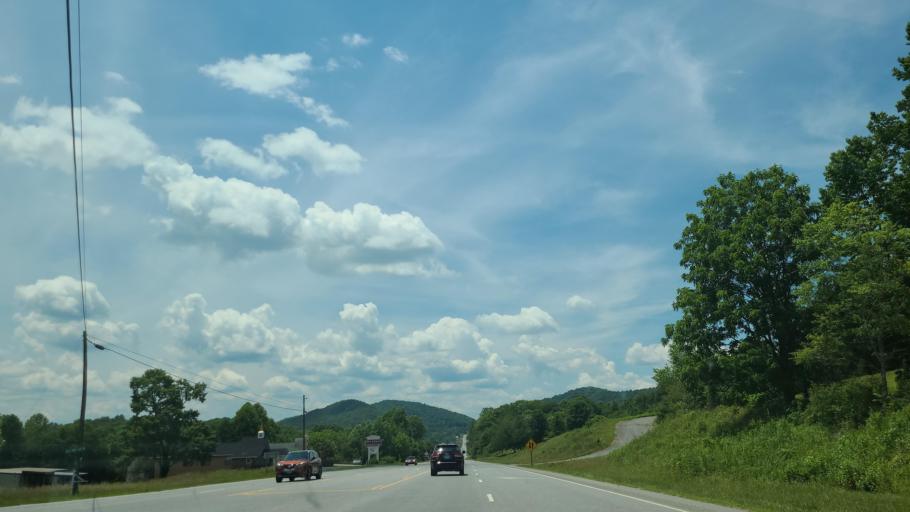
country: US
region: North Carolina
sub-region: Clay County
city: Hayesville
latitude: 35.0355
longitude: -83.8332
